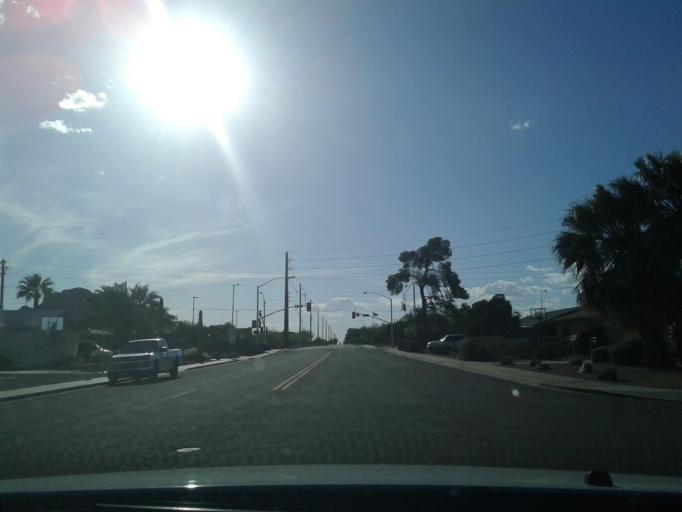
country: US
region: Arizona
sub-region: Maricopa County
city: Scottsdale
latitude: 33.4730
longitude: -111.9423
